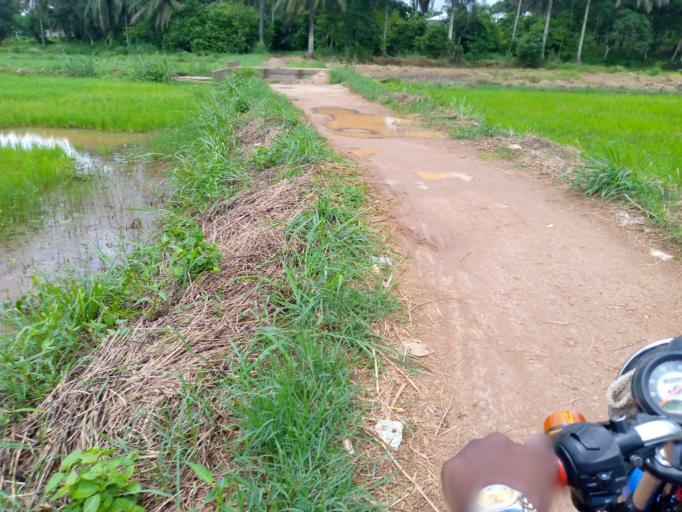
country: SL
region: Eastern Province
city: Kenema
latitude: 7.8767
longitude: -11.1665
